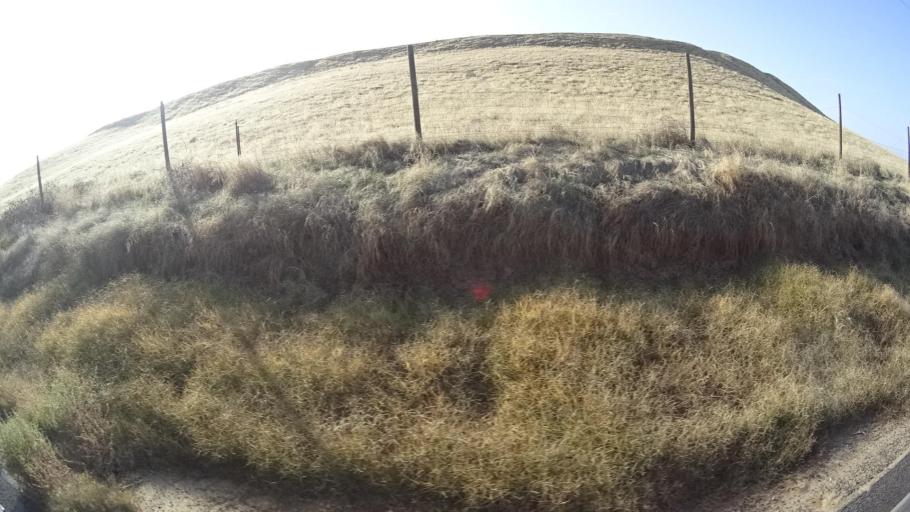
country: US
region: California
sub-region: Tulare County
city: Richgrove
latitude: 35.6619
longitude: -119.0885
